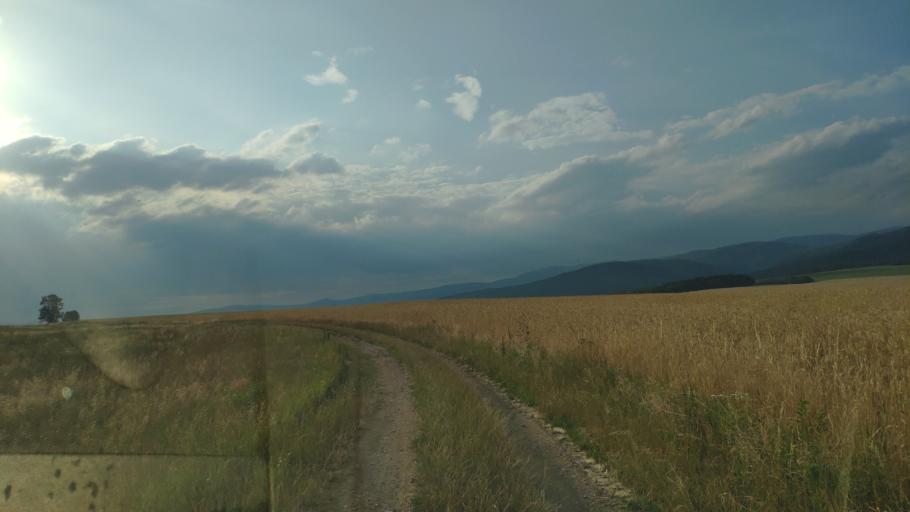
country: SK
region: Kosicky
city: Moldava nad Bodvou
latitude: 48.6947
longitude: 20.9972
